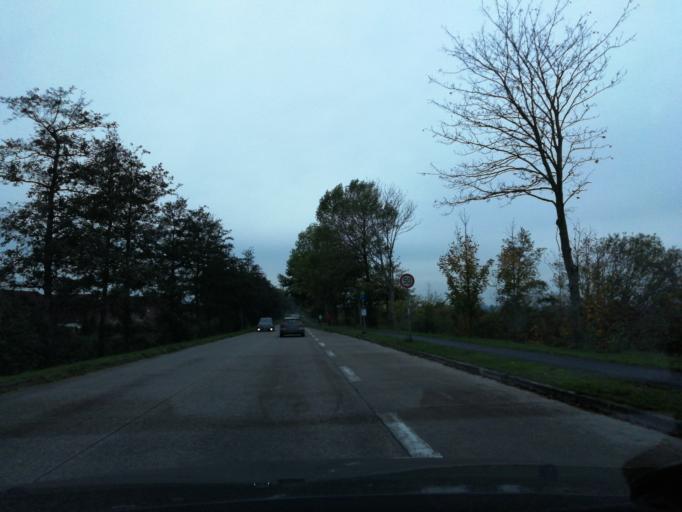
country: DE
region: Lower Saxony
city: Schillig
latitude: 53.6393
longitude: 8.0344
